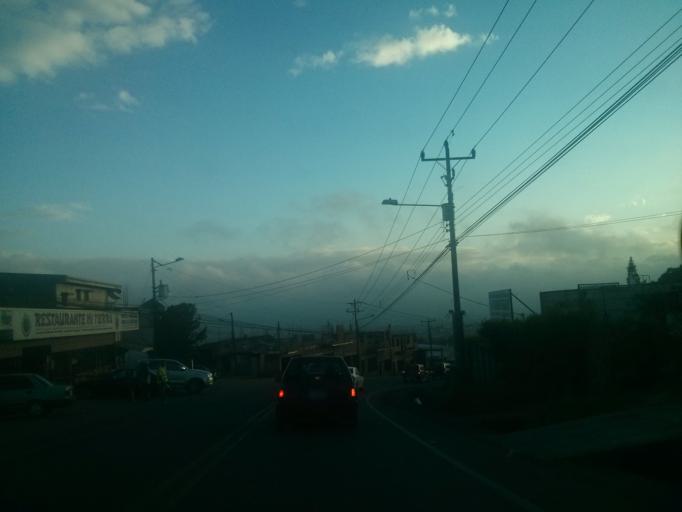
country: CR
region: Cartago
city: Cartago
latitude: 9.8789
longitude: -83.9014
